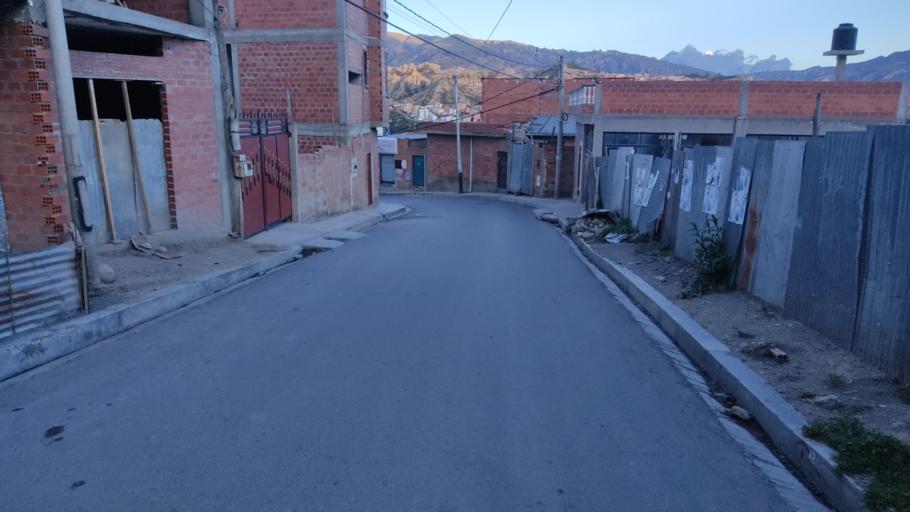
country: BO
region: La Paz
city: La Paz
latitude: -16.5069
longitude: -68.0928
